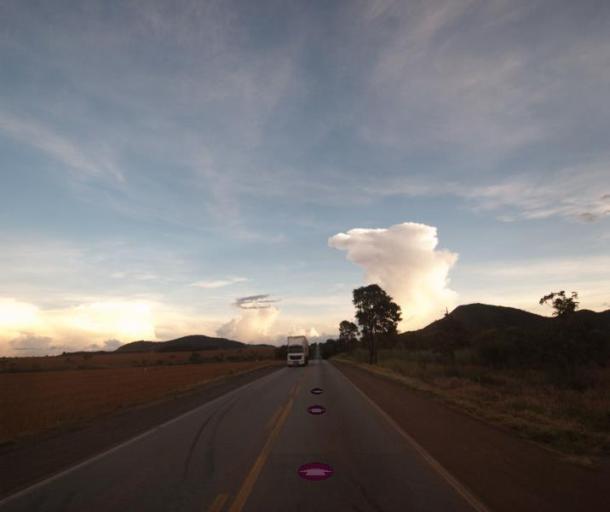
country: BR
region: Goias
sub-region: Uruacu
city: Uruacu
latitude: -14.3730
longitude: -49.1582
